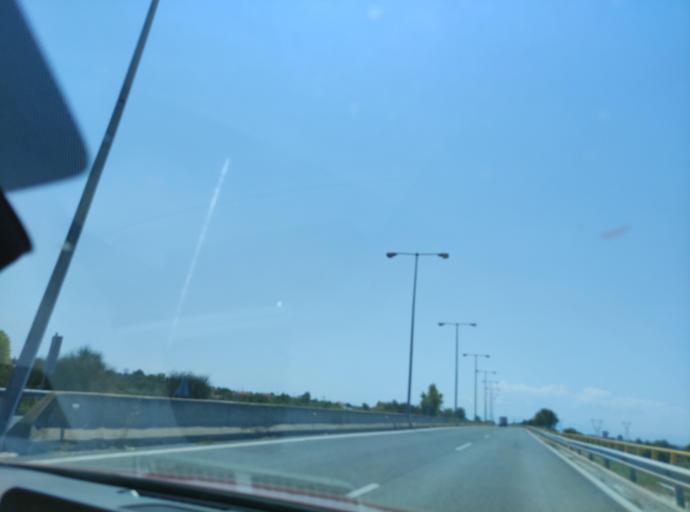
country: GR
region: Central Macedonia
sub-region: Nomos Serron
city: Vamvakofyto
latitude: 41.1575
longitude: 23.4043
